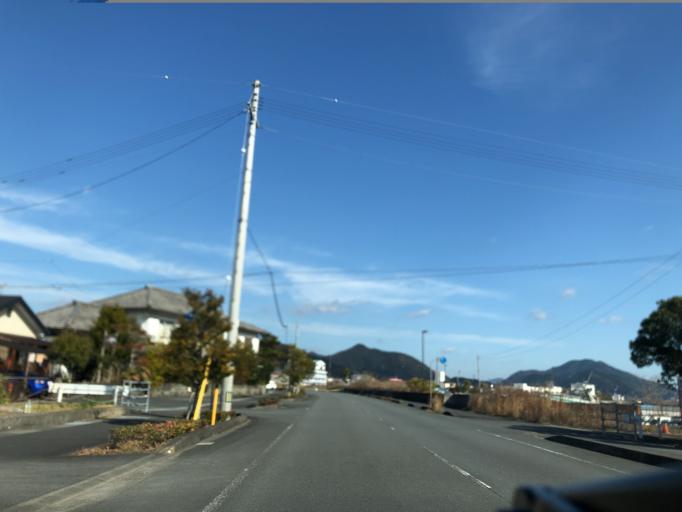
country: JP
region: Kochi
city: Sukumo
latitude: 32.9229
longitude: 132.7020
